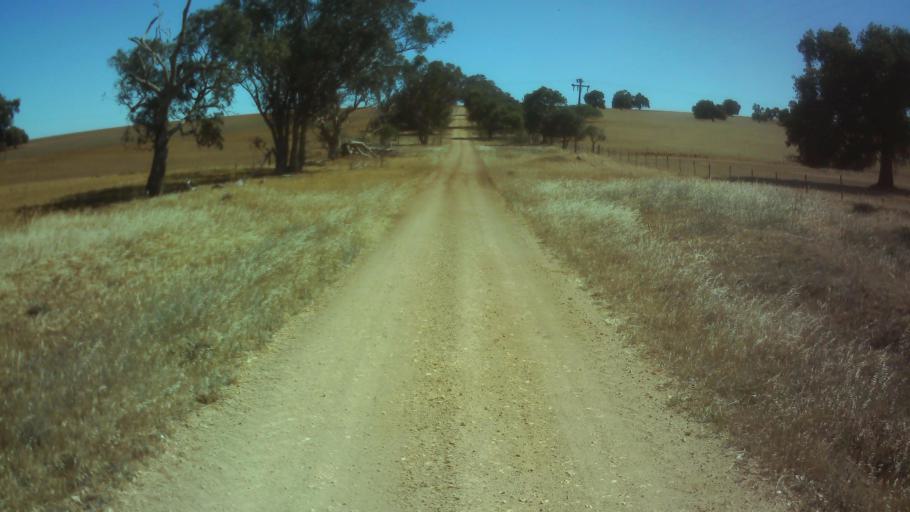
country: AU
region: New South Wales
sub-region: Weddin
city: Grenfell
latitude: -33.9811
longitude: 148.3418
